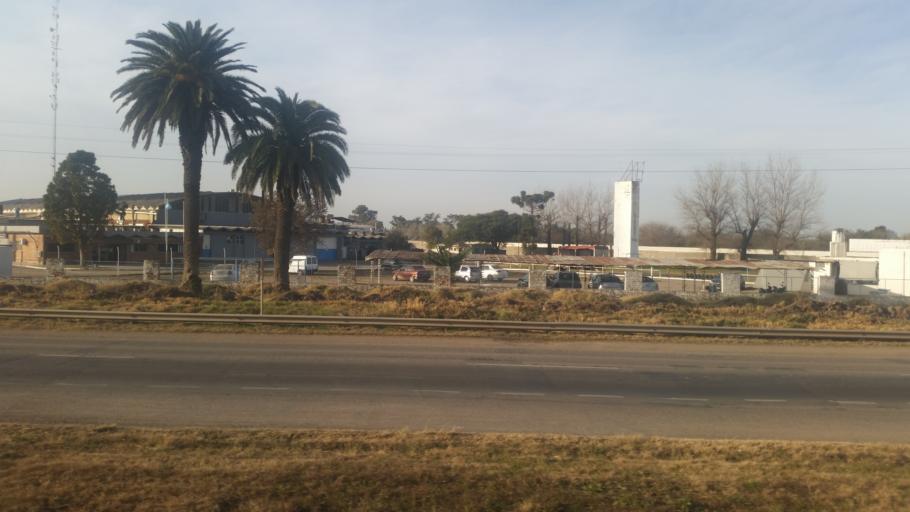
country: AR
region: Cordoba
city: Toledo
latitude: -31.4847
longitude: -64.0828
